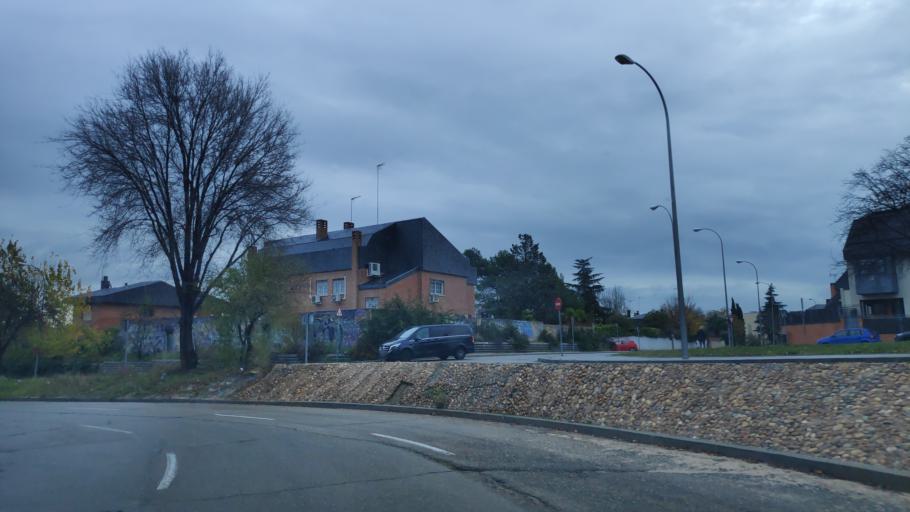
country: ES
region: Madrid
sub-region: Provincia de Madrid
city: San Blas
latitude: 40.4551
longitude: -3.6168
